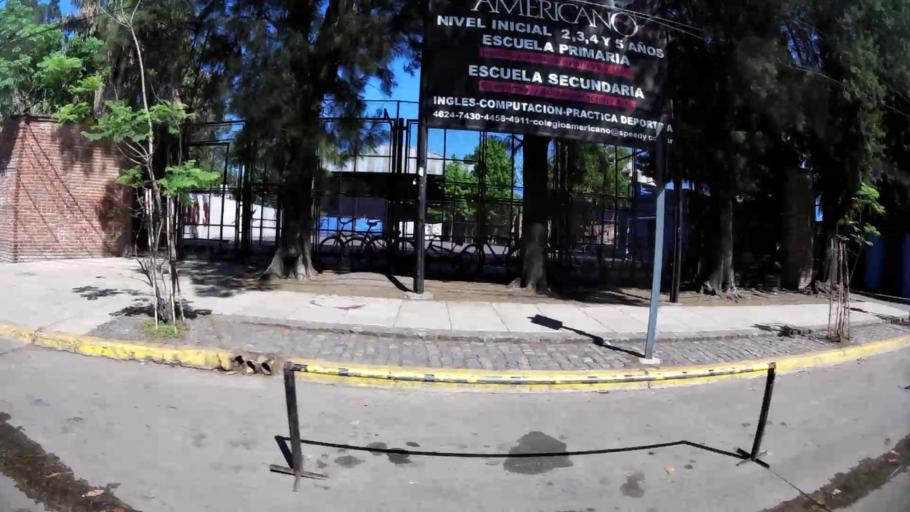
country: AR
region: Buenos Aires
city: Ituzaingo
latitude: -34.6338
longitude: -58.6541
